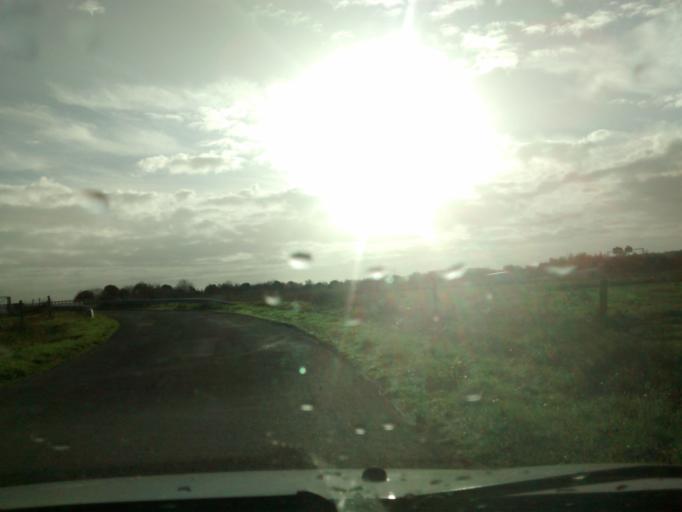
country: FR
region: Brittany
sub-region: Departement d'Ille-et-Vilaine
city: Cesson-Sevigne
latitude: 48.1255
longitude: -1.5755
